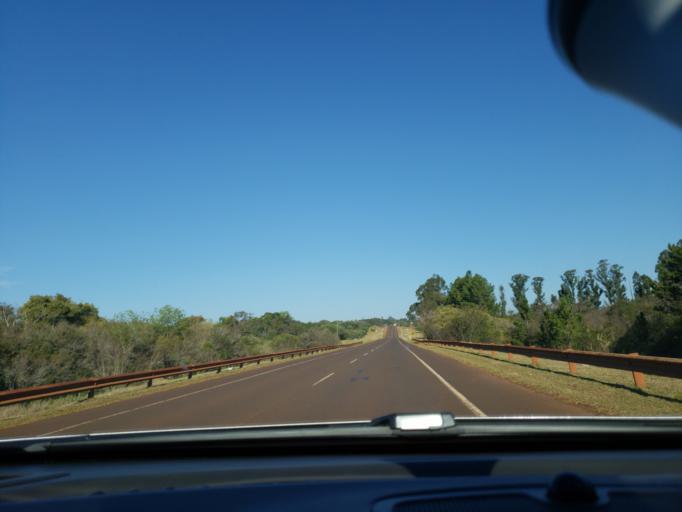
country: AR
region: Misiones
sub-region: Departamento de Apostoles
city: Apostoles
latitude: -27.8454
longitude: -55.7655
